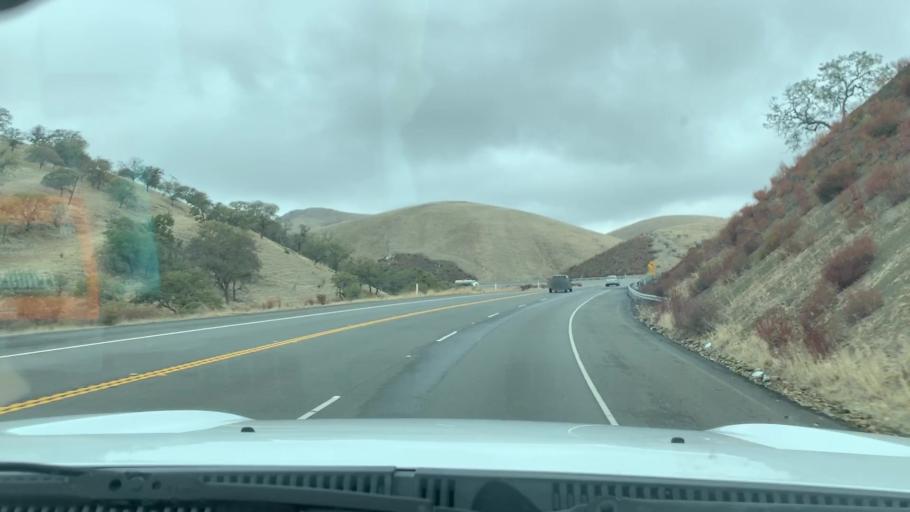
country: US
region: California
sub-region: San Luis Obispo County
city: Shandon
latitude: 35.7812
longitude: -120.1983
